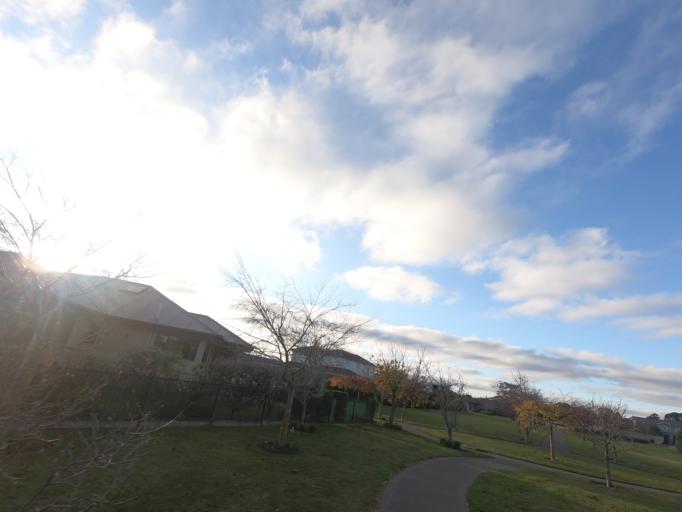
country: NZ
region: Canterbury
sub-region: Selwyn District
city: Prebbleton
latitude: -43.5681
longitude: 172.5661
